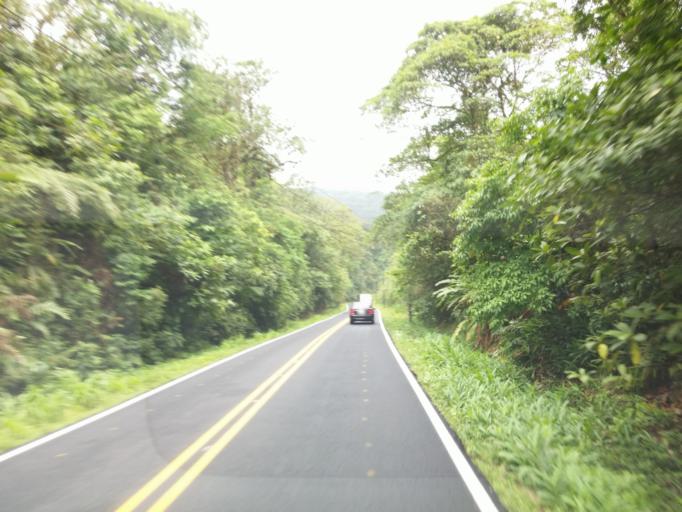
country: CR
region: Alajuela
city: San Ramon
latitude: 10.2019
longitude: -84.5321
